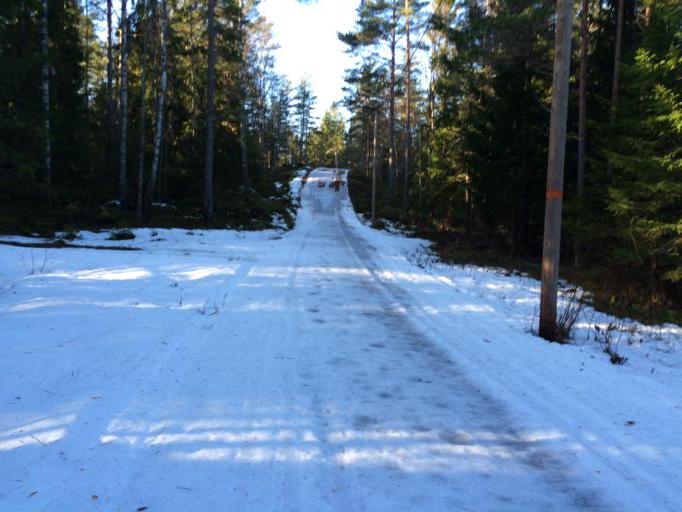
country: SE
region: Vaestmanland
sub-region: Hallstahammars Kommun
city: Hallstahammar
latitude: 59.6348
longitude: 16.2585
